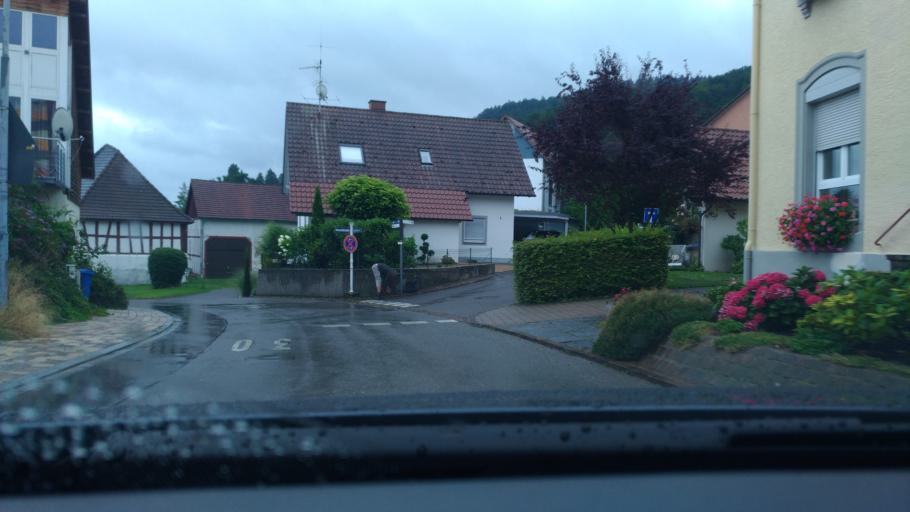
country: DE
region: Baden-Wuerttemberg
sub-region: Freiburg Region
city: Bodman-Ludwigshafen
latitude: 47.7976
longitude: 9.0403
